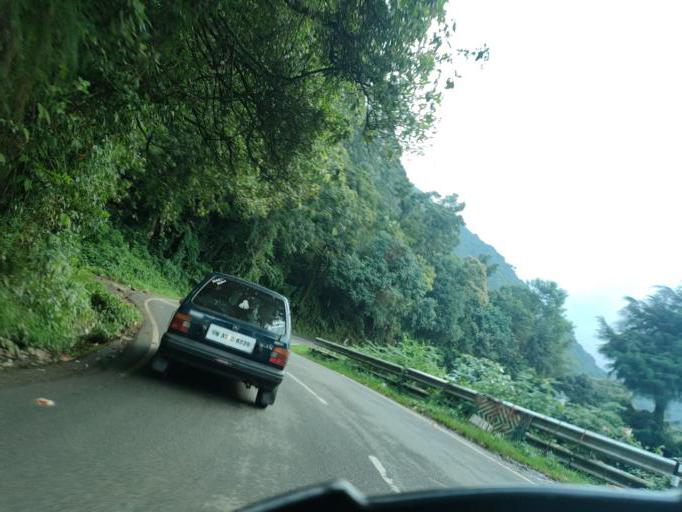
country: IN
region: Tamil Nadu
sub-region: Dindigul
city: Kodaikanal
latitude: 10.2583
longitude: 77.5324
